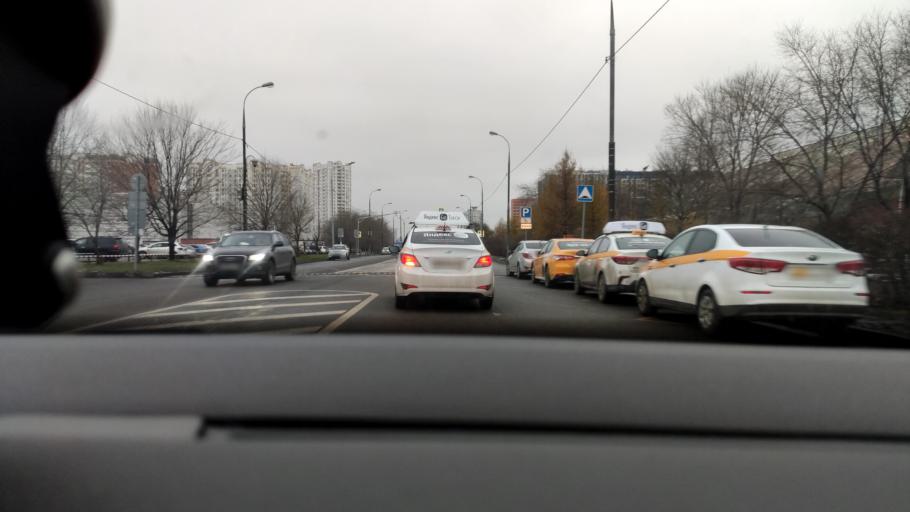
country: RU
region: Moscow
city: Lyublino
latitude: 55.6722
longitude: 37.7828
